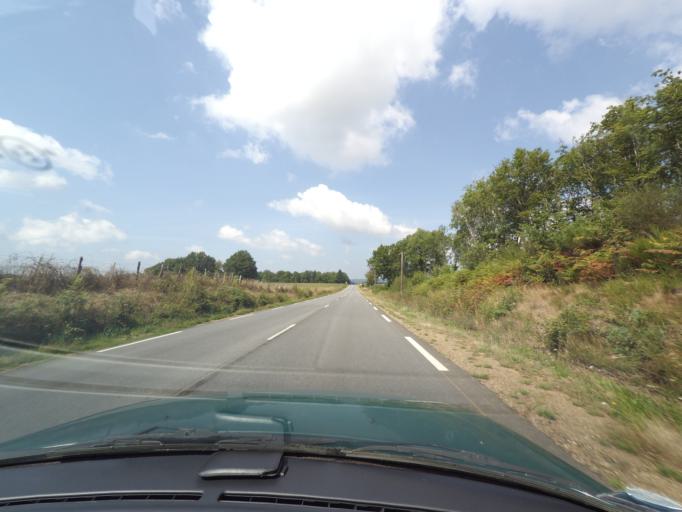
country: FR
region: Limousin
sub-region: Departement de la Haute-Vienne
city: Neuvic-Entier
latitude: 45.7294
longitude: 1.6485
